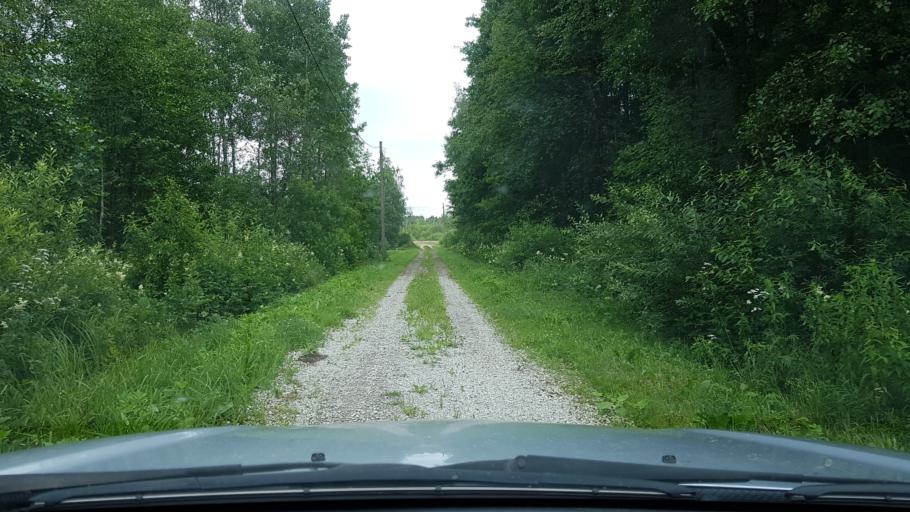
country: EE
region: Ida-Virumaa
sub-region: Narva-Joesuu linn
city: Narva-Joesuu
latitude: 59.3697
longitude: 28.0531
